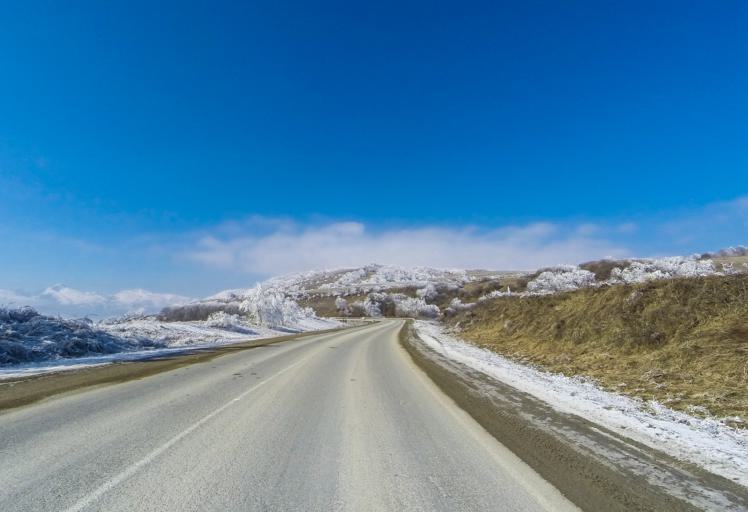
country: RU
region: Kabardino-Balkariya
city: Zhemtala
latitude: 43.3418
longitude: 43.6695
